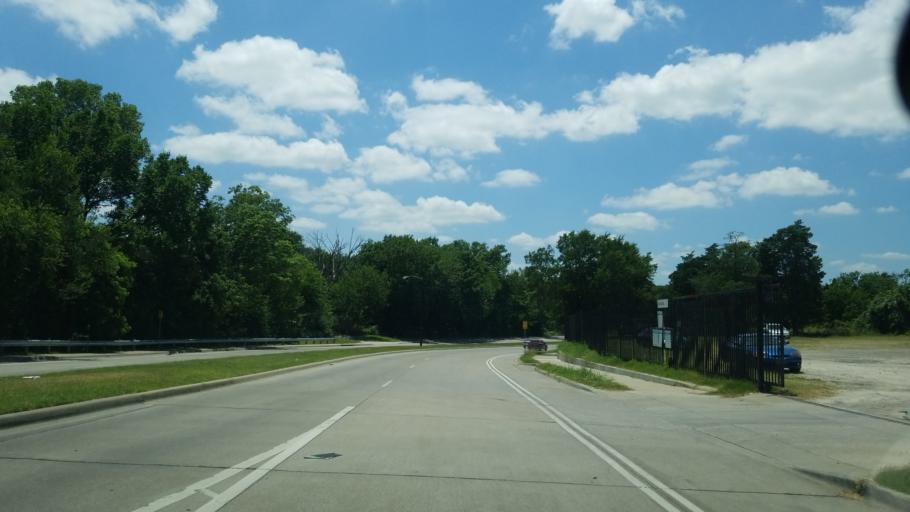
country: US
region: Texas
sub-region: Dallas County
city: Hutchins
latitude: 32.7330
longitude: -96.7147
